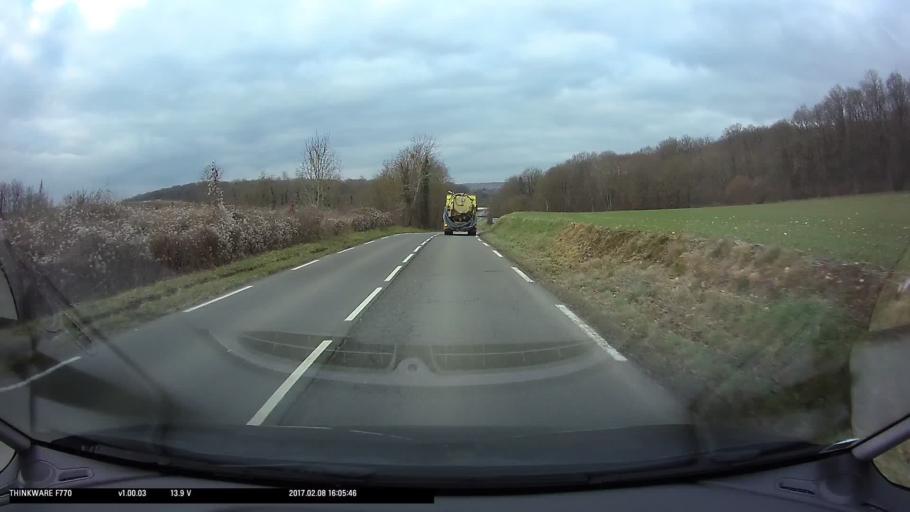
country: FR
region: Ile-de-France
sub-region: Departement du Val-d'Oise
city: Marines
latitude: 49.1285
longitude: 1.9824
